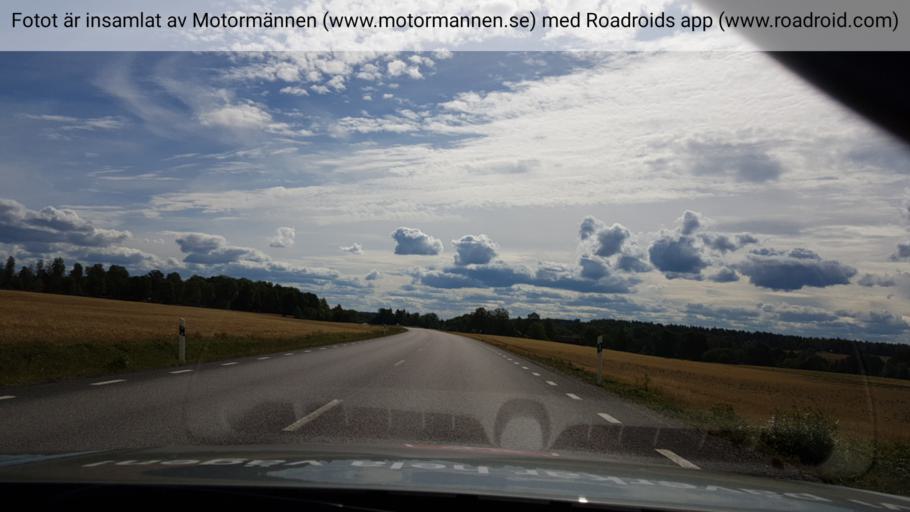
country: SE
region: Uppsala
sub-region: Osthammars Kommun
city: Bjorklinge
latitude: 59.9496
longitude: 17.4095
